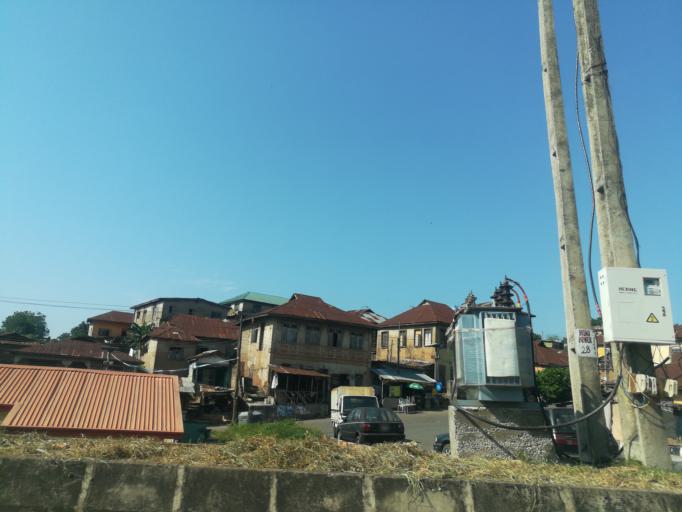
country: NG
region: Ogun
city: Abeokuta
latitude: 7.1569
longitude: 3.3354
